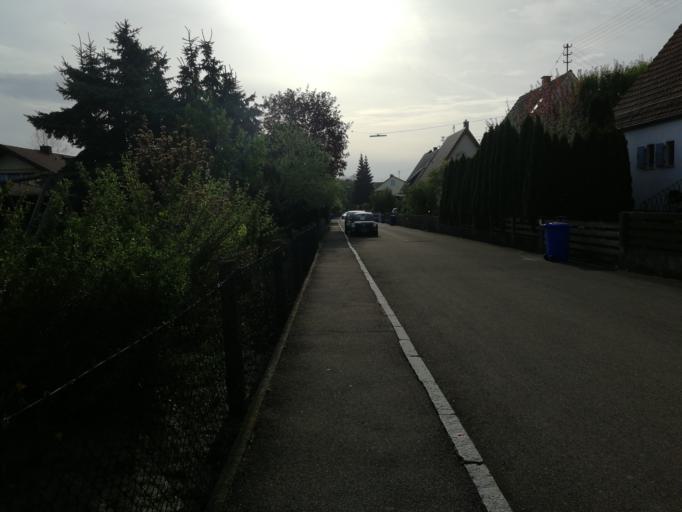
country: DE
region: Bavaria
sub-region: Swabia
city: Wertingen
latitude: 48.5639
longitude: 10.6756
